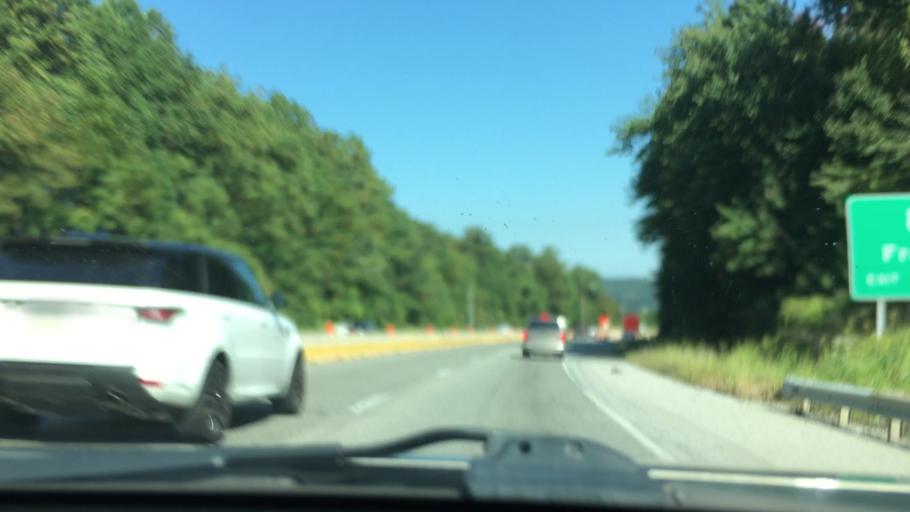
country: US
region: Pennsylvania
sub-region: Chester County
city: Exton
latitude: 40.0240
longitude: -75.5885
